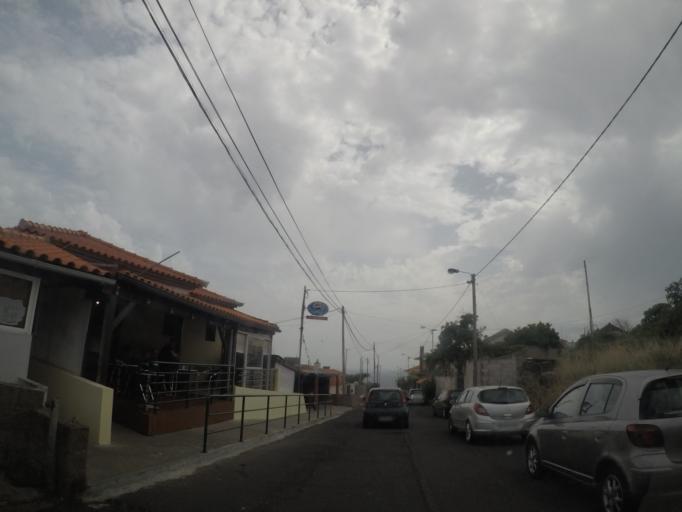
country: PT
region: Madeira
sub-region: Santa Cruz
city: Santa Cruz
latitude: 32.6577
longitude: -16.8147
